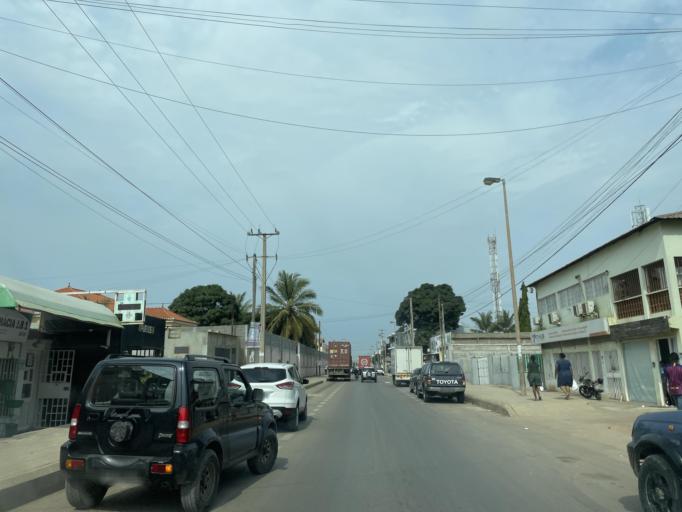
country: AO
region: Luanda
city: Luanda
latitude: -8.8975
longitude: 13.1887
